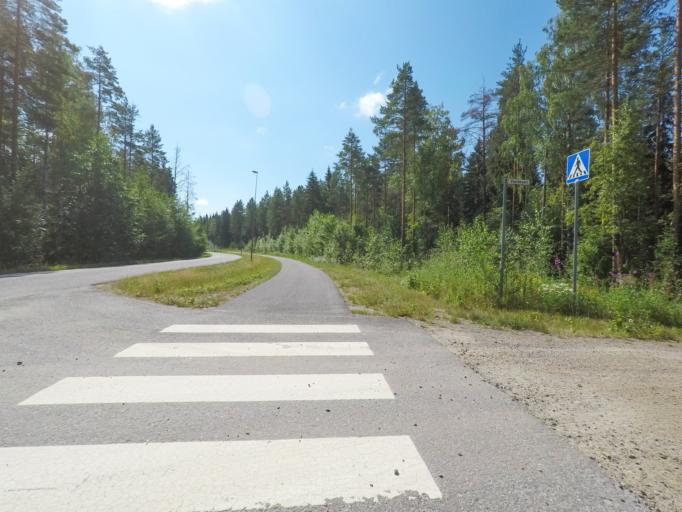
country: FI
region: Southern Savonia
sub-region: Mikkeli
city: Puumala
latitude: 61.5140
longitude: 28.1640
